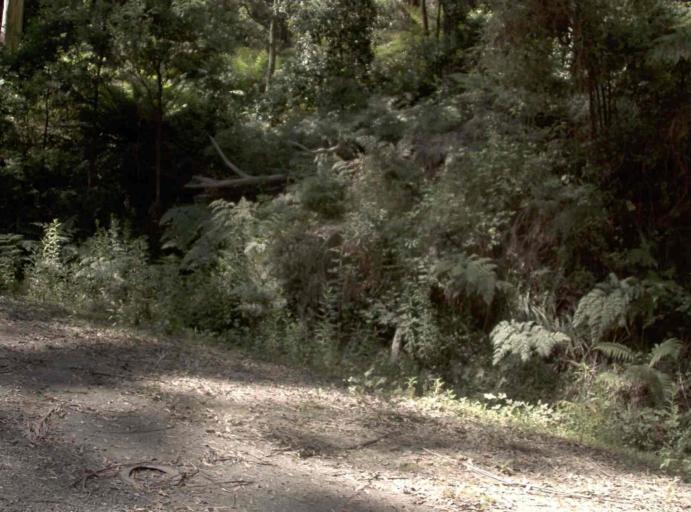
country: AU
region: New South Wales
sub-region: Bombala
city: Bombala
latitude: -37.2511
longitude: 148.7517
